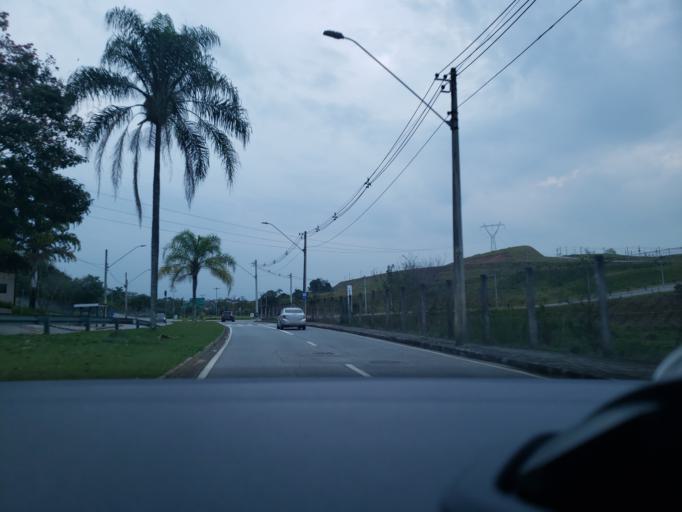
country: BR
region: Sao Paulo
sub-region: Sao Jose Dos Campos
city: Sao Jose dos Campos
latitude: -23.1913
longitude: -45.9359
